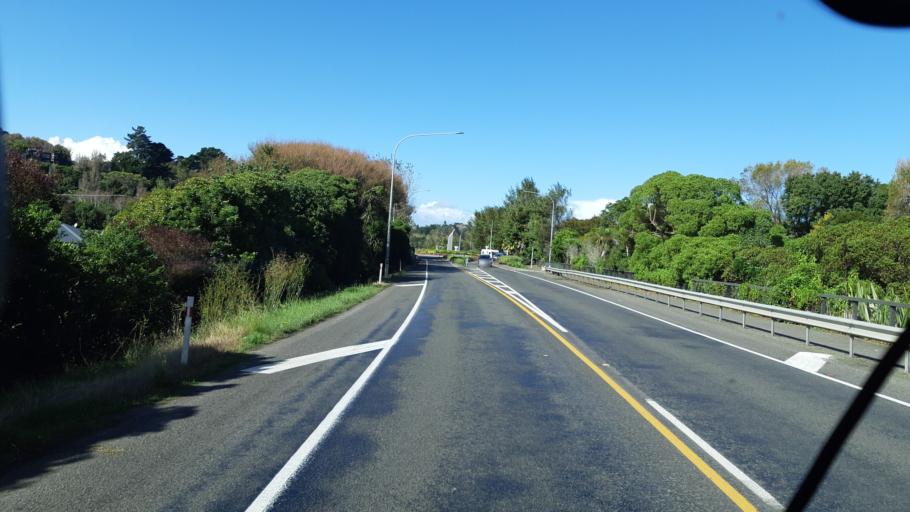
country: NZ
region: Manawatu-Wanganui
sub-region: Wanganui District
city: Wanganui
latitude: -39.9475
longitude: 175.0494
